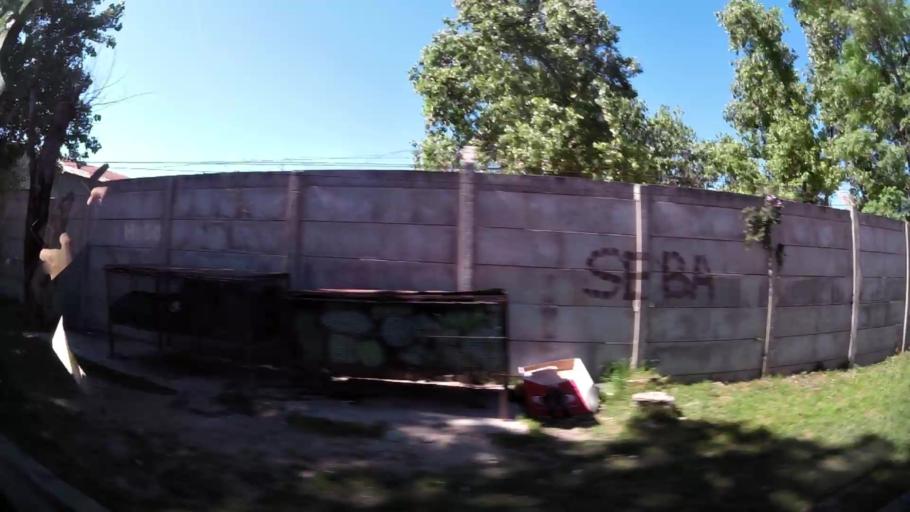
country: AR
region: Buenos Aires
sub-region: Partido de Tigre
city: Tigre
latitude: -34.4989
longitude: -58.6084
